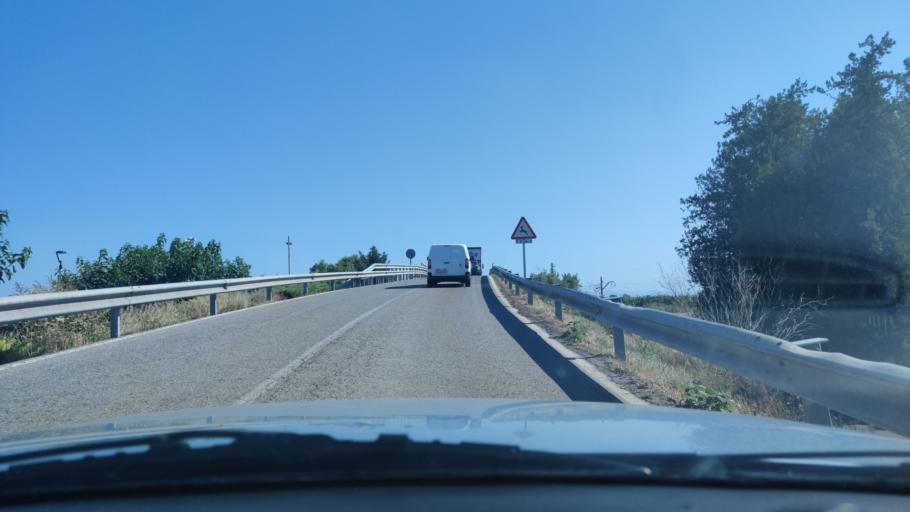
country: ES
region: Catalonia
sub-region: Provincia de Lleida
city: Sidamon
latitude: 41.6308
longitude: 0.7866
